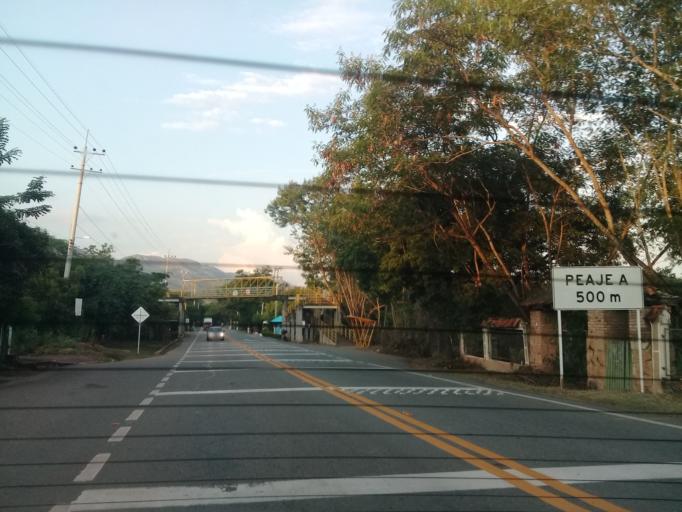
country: CO
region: Cundinamarca
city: Agua de Dios
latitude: 4.3988
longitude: -74.7344
